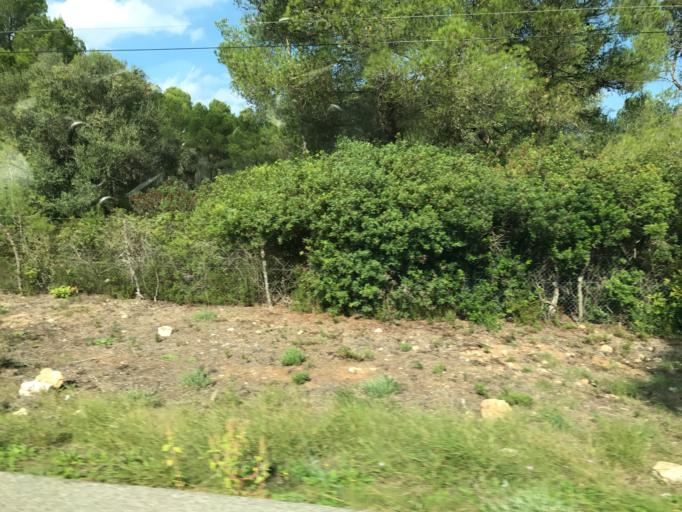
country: ES
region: Balearic Islands
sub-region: Illes Balears
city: Santa Margalida
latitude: 39.7299
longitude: 3.1931
